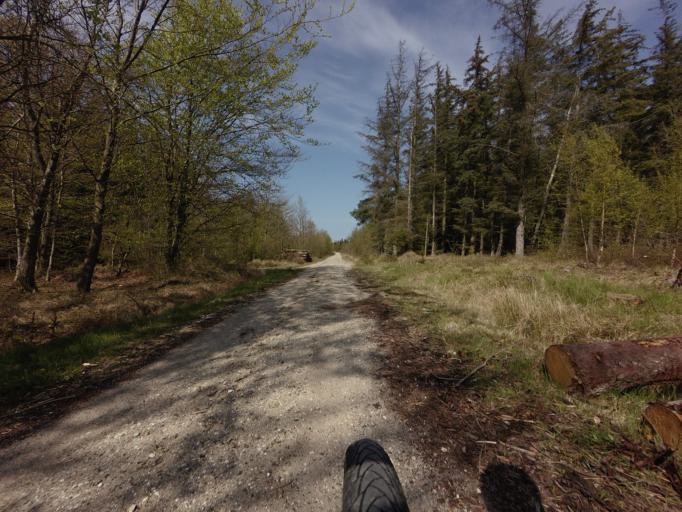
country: DK
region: North Denmark
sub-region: Jammerbugt Kommune
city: Brovst
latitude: 57.1959
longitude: 9.5387
